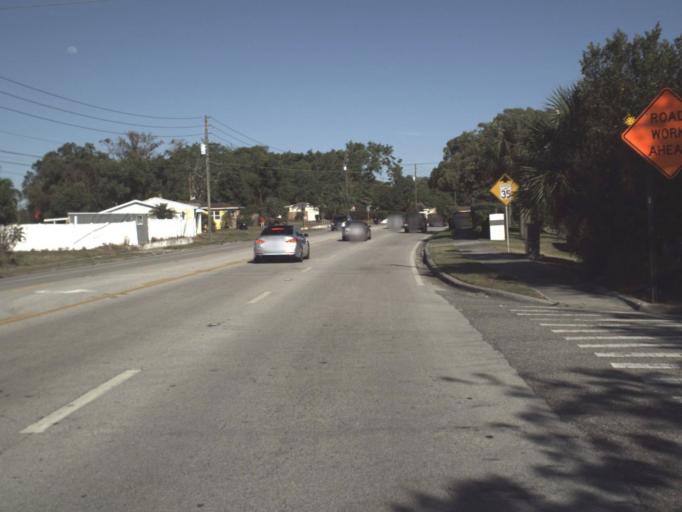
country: US
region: Florida
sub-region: Orange County
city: Fairview Shores
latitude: 28.5961
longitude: -81.3891
